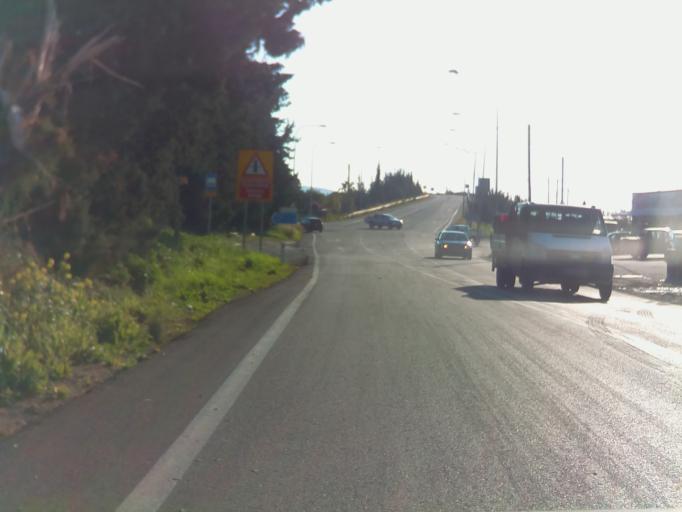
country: CY
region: Pafos
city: Paphos
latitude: 34.7235
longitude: 32.5262
